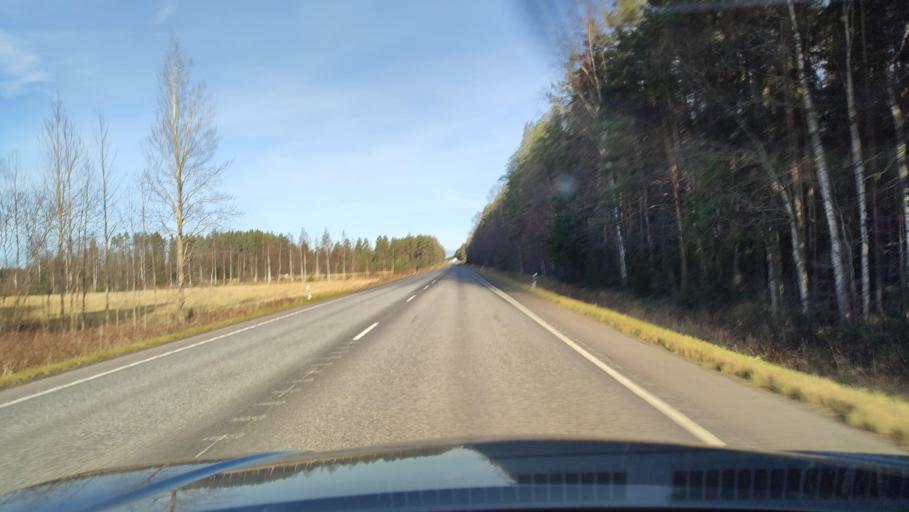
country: FI
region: Ostrobothnia
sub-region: Vaasa
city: Malax
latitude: 62.8092
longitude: 21.6815
